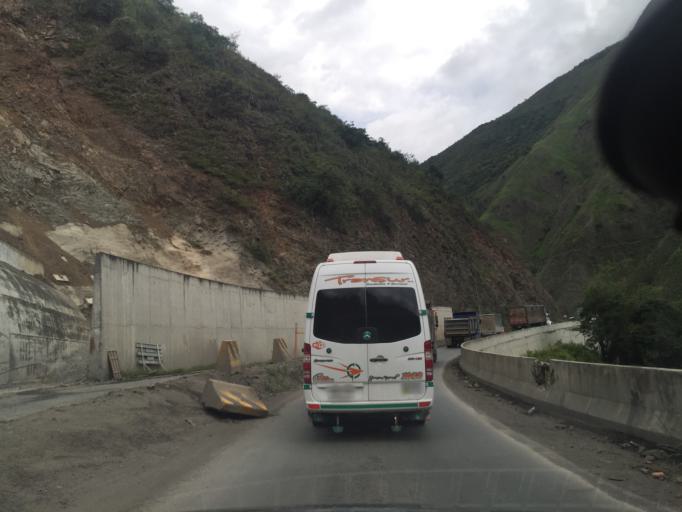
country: CO
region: Valle del Cauca
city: Dagua
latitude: 3.7761
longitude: -76.6992
